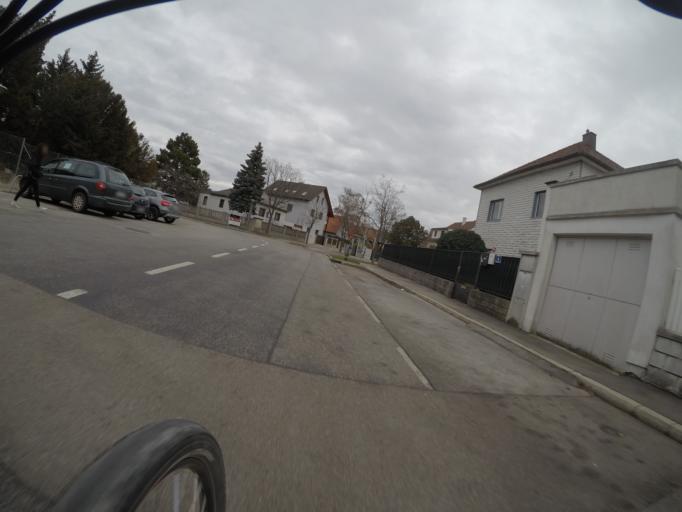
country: AT
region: Lower Austria
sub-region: Politischer Bezirk Modling
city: Vosendorf
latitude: 48.1350
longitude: 16.3259
